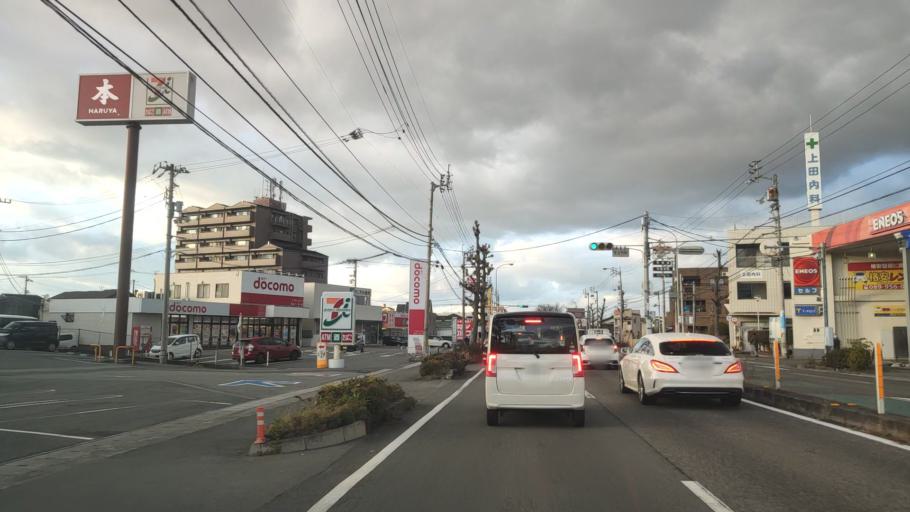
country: JP
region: Ehime
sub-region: Shikoku-chuo Shi
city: Matsuyama
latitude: 33.8040
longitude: 132.7825
